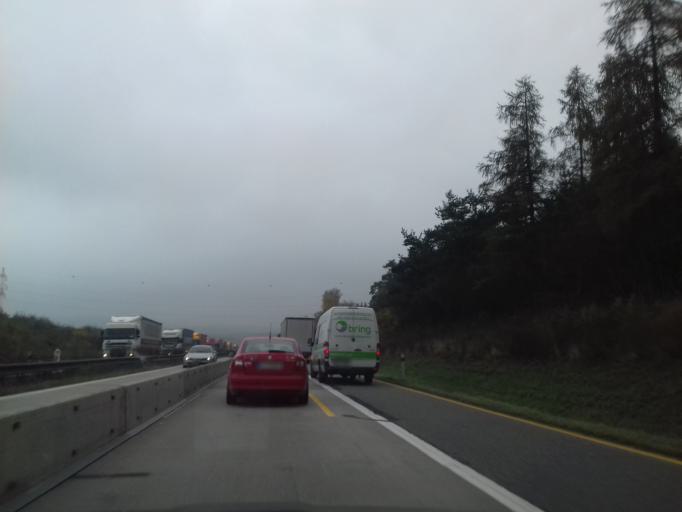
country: CZ
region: Vysocina
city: Dobronin
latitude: 49.4421
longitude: 15.6322
